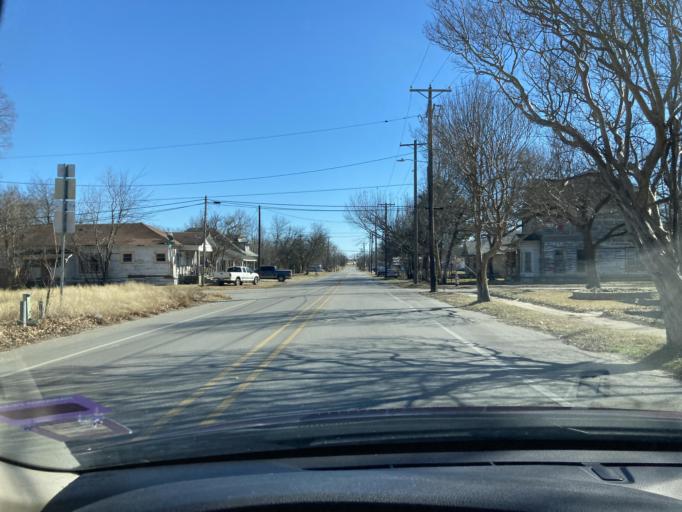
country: US
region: Texas
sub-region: Navarro County
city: Corsicana
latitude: 32.0863
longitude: -96.4659
